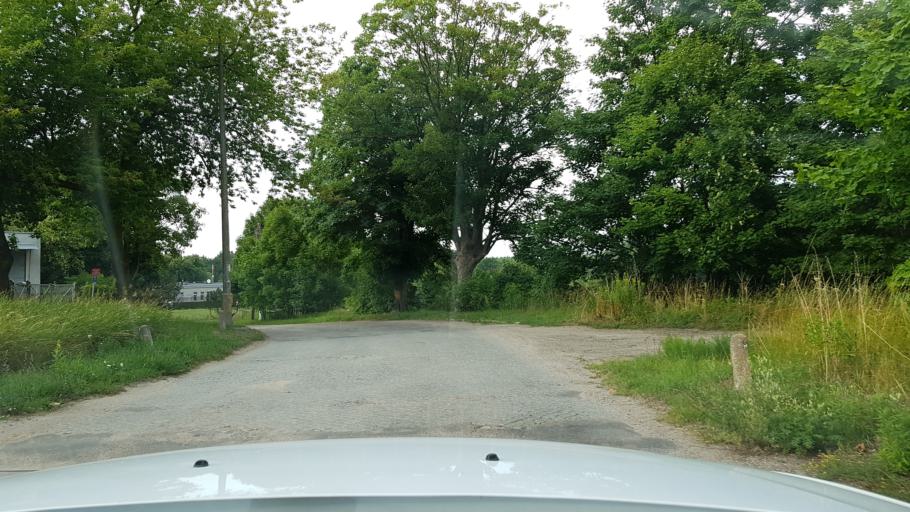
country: PL
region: West Pomeranian Voivodeship
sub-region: Powiat swidwinski
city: Polczyn-Zdroj
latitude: 53.7742
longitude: 16.0936
